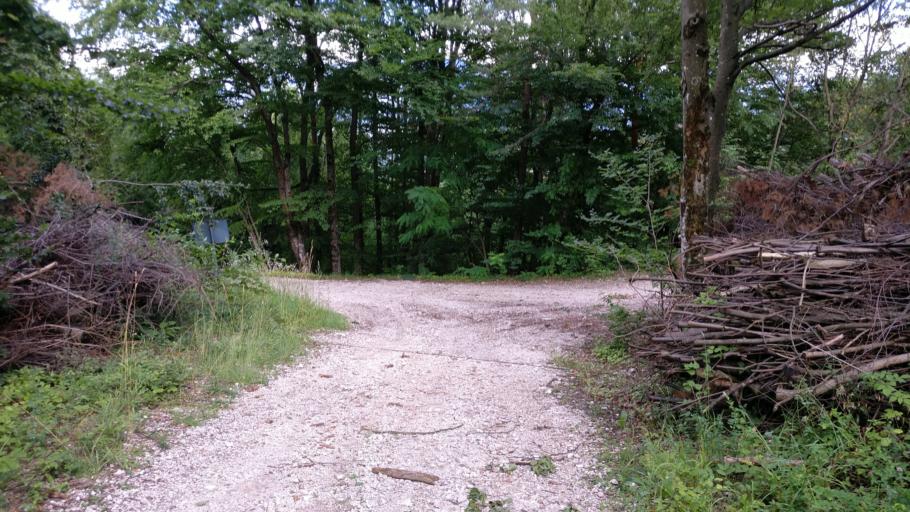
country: IT
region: Trentino-Alto Adige
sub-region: Bolzano
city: San Michele
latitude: 46.4534
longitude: 11.2375
